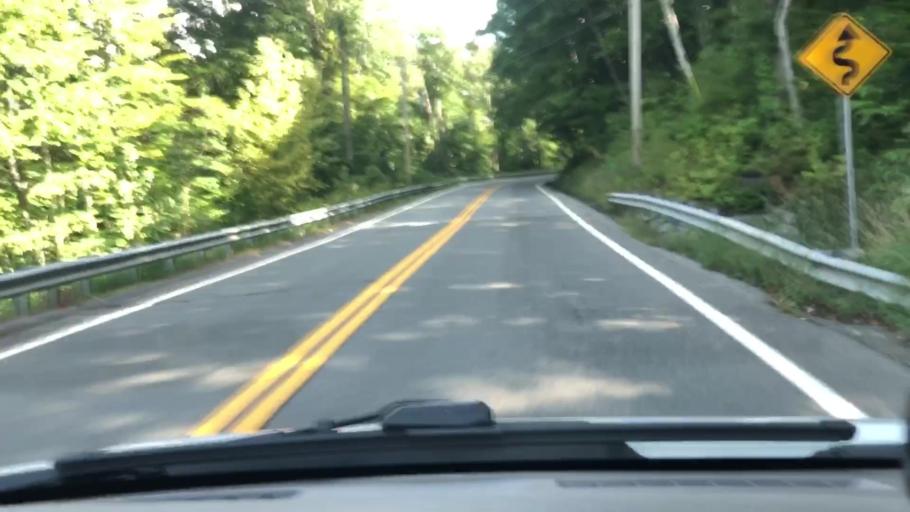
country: US
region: Massachusetts
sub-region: Berkshire County
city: North Adams
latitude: 42.7041
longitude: -73.0679
